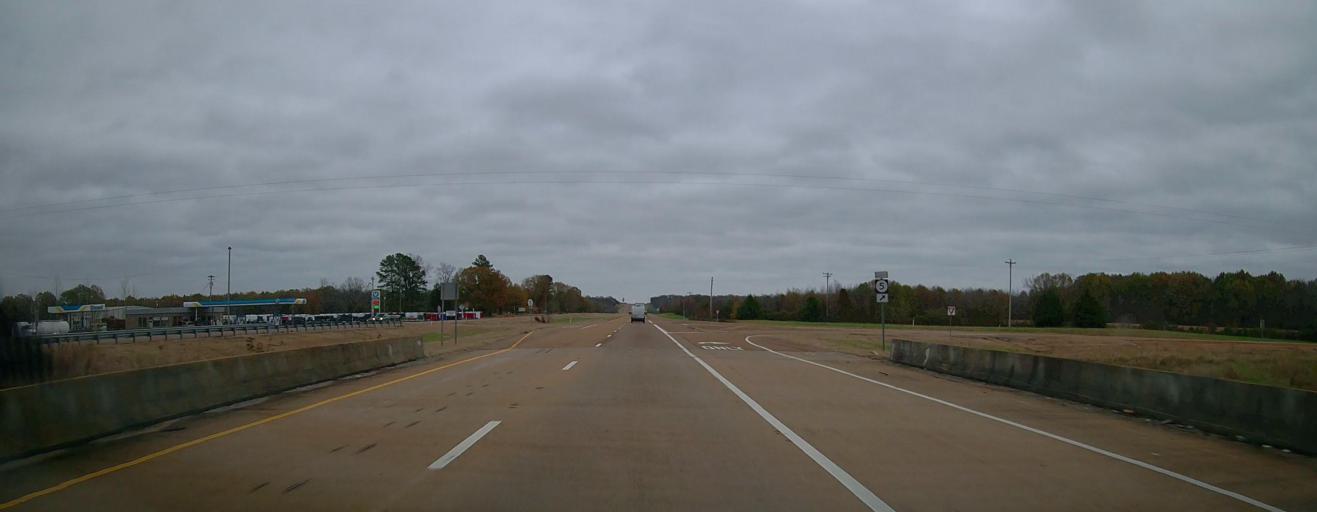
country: US
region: Mississippi
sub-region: Benton County
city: Ashland
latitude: 34.9461
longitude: -89.2125
